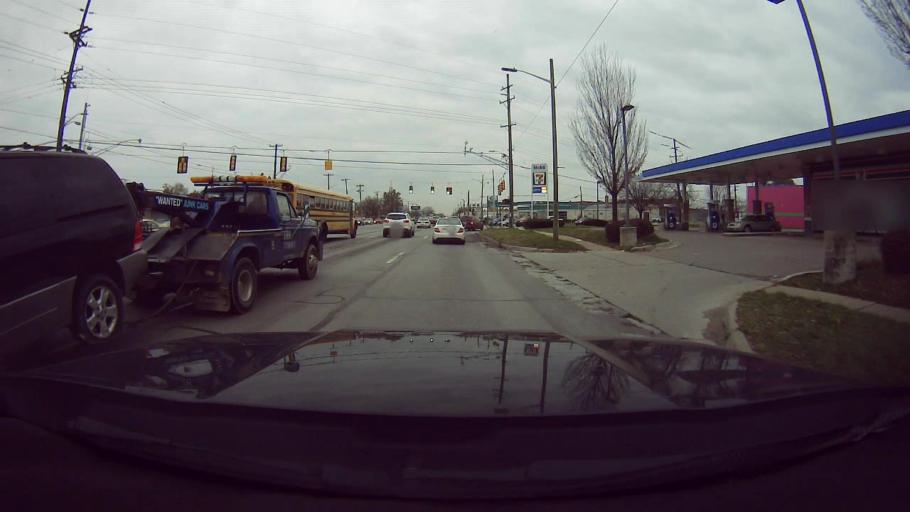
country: US
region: Michigan
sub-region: Macomb County
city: Eastpointe
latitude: 42.4791
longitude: -82.9804
